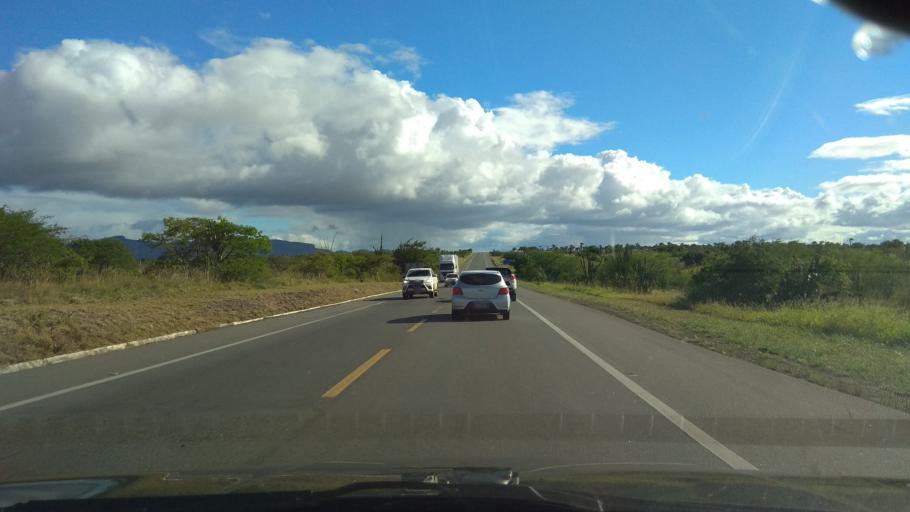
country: BR
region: Bahia
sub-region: Castro Alves
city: Castro Alves
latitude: -12.6708
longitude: -39.6505
